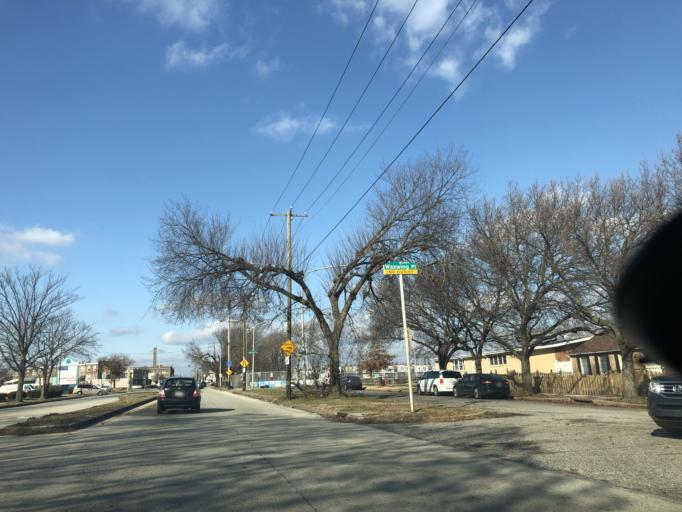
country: US
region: Pennsylvania
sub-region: Delaware County
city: Colwyn
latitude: 39.9127
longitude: -75.2320
